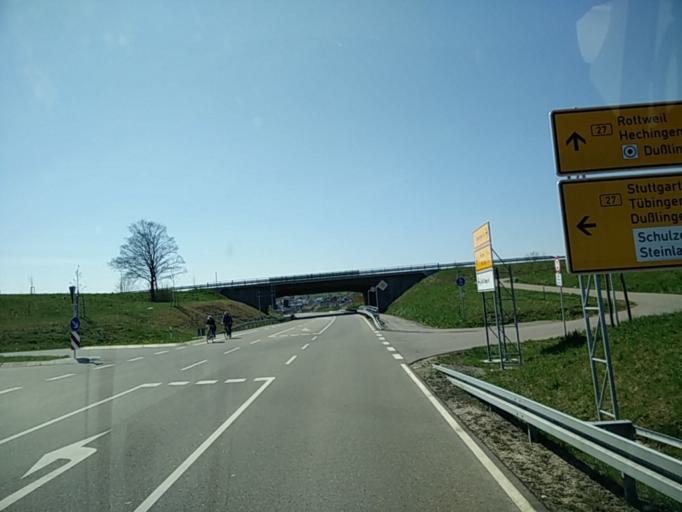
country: DE
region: Baden-Wuerttemberg
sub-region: Tuebingen Region
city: Dusslingen
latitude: 48.4575
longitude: 9.0639
